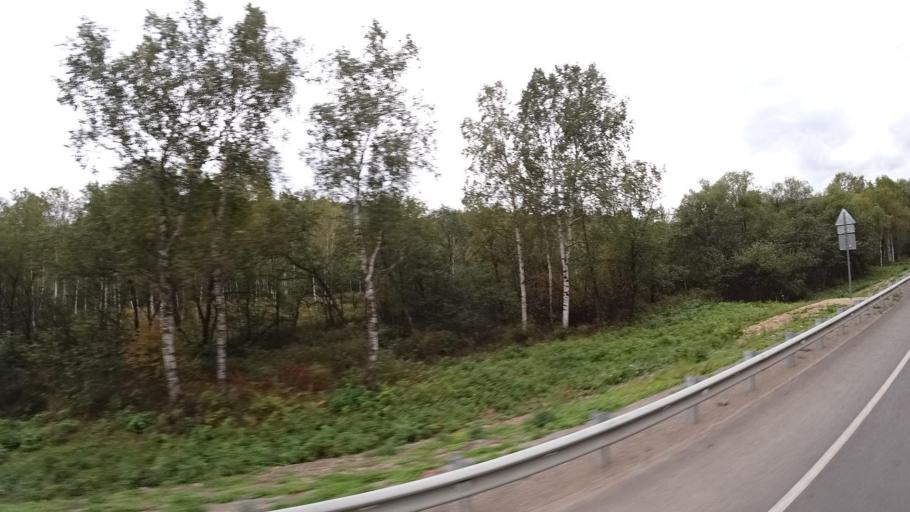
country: RU
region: Jewish Autonomous Oblast
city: Khingansk
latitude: 48.9834
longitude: 131.1543
